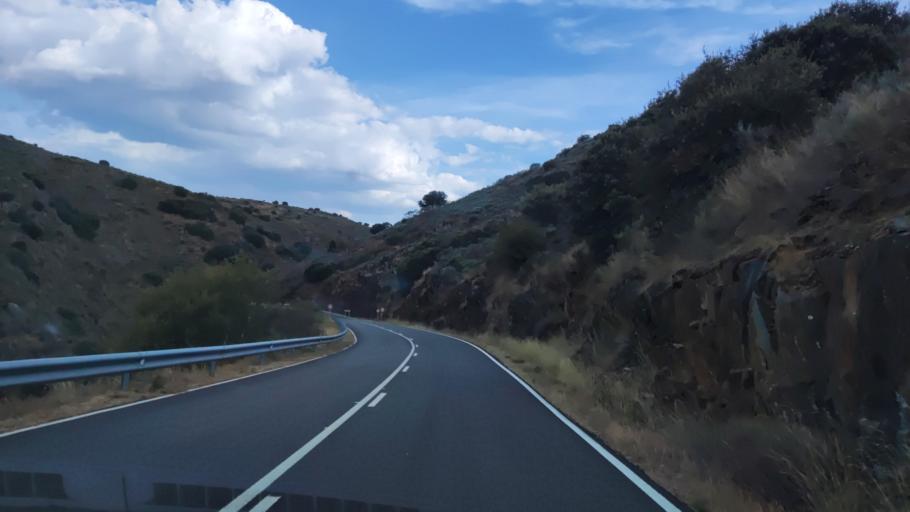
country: ES
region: Castille and Leon
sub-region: Provincia de Salamanca
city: Pastores
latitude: 40.4966
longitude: -6.4933
